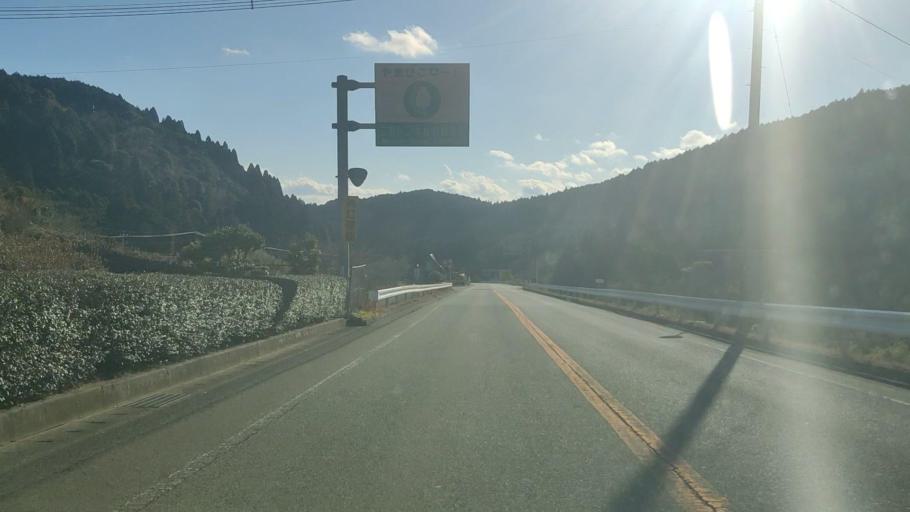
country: JP
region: Fukuoka
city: Maebaru-chuo
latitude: 33.4619
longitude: 130.2748
